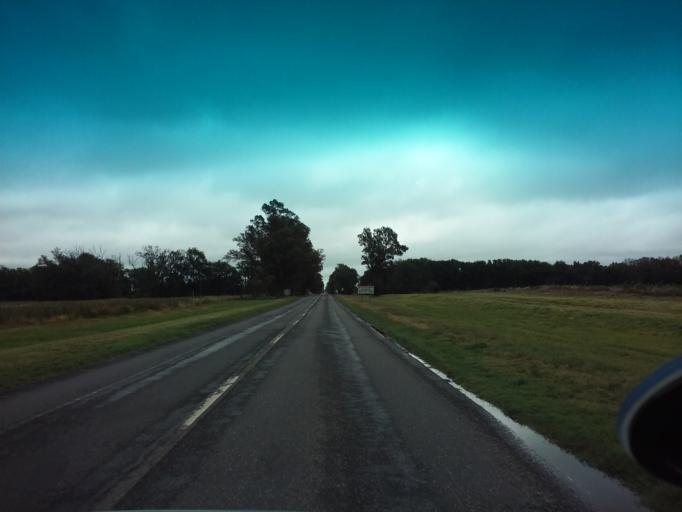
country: AR
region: La Pampa
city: Catrilo
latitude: -36.4100
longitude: -63.3812
